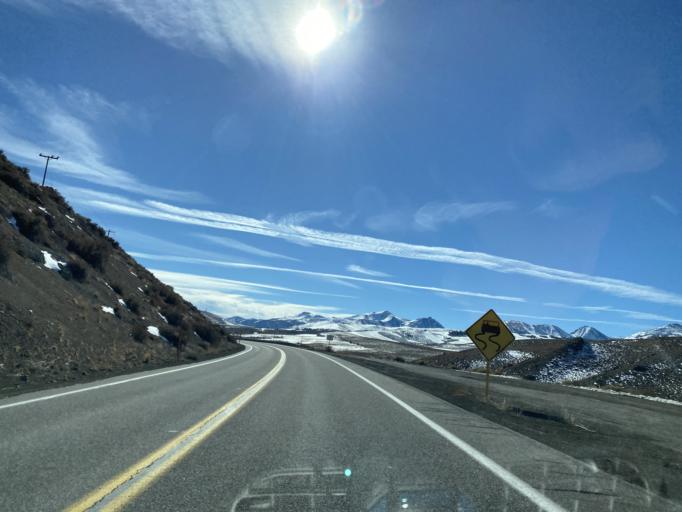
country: US
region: California
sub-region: Mono County
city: Bridgeport
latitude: 38.1289
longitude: -119.1827
